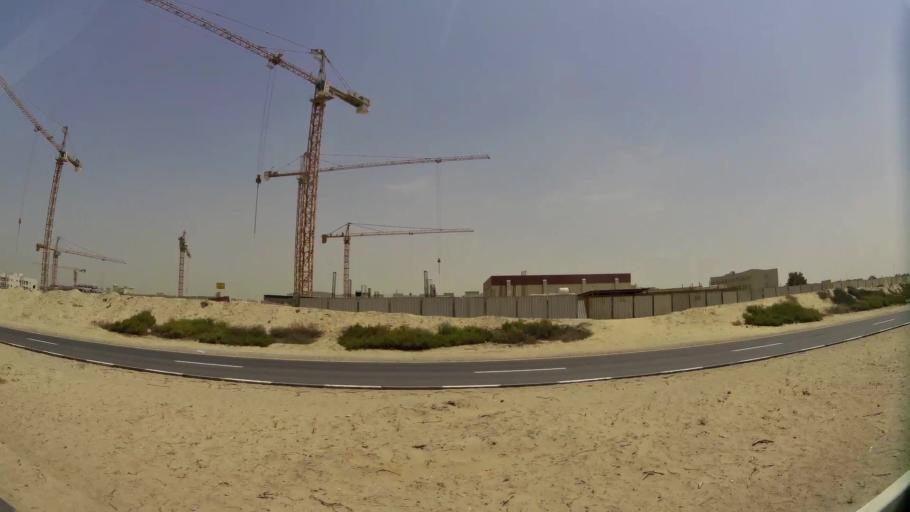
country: AE
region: Ash Shariqah
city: Sharjah
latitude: 25.2739
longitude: 55.4087
